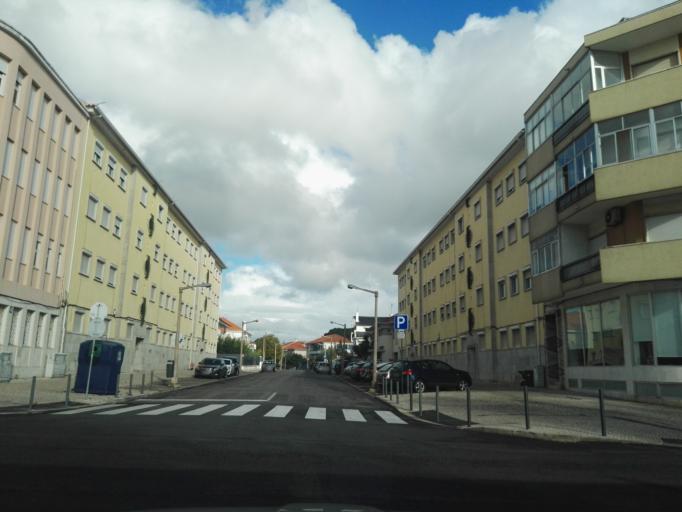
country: PT
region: Lisbon
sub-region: Lisbon
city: Lisbon
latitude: 38.7528
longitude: -9.1380
